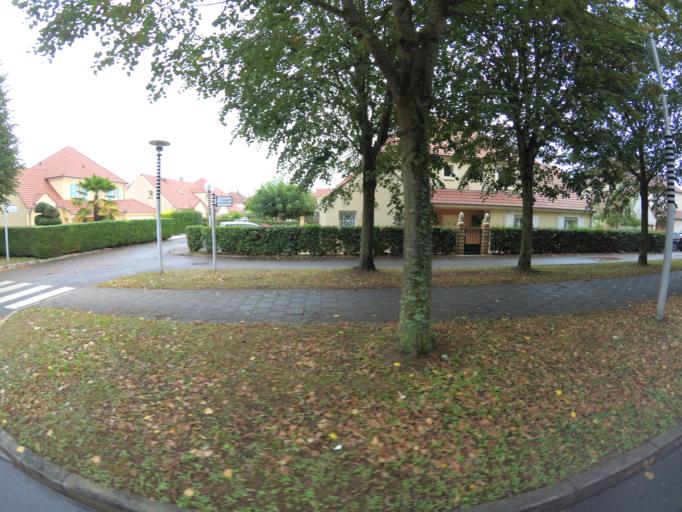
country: FR
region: Ile-de-France
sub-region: Departement de Seine-et-Marne
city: Conches-sur-Gondoire
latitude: 48.8432
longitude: 2.7261
